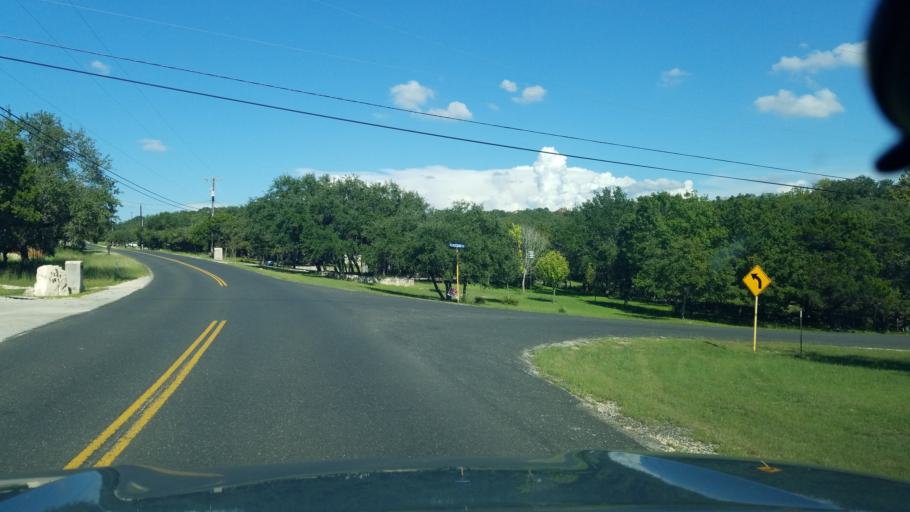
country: US
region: Texas
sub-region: Bexar County
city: Timberwood Park
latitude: 29.6685
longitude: -98.5154
